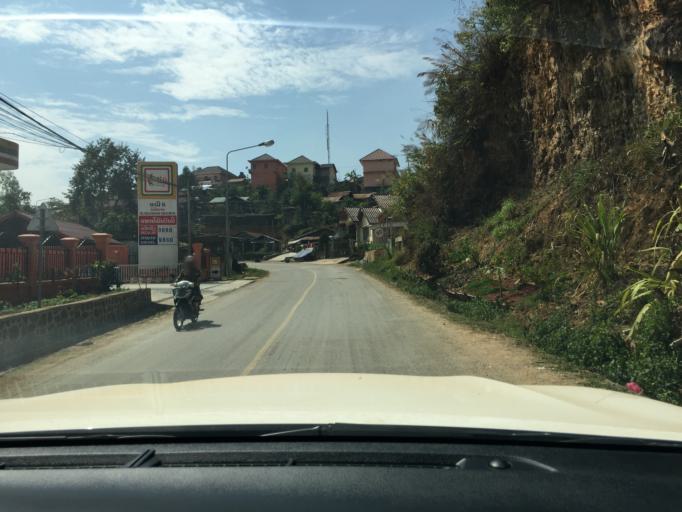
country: LA
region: Phongsali
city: Phongsali
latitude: 21.6809
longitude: 102.0971
